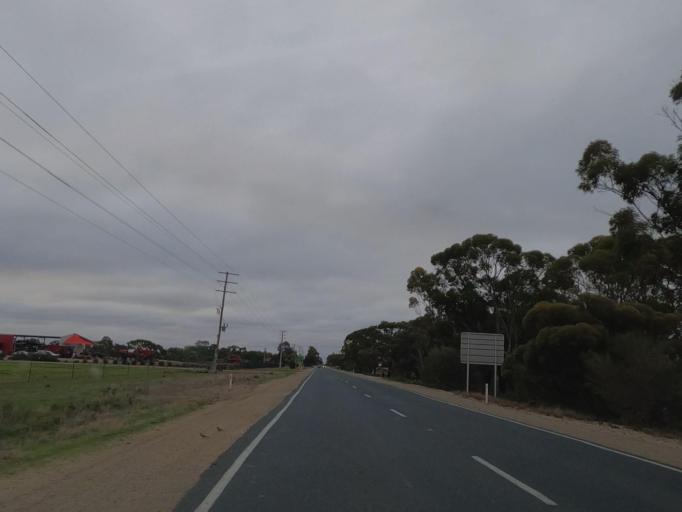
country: AU
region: Victoria
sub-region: Swan Hill
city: Swan Hill
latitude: -35.3889
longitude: 143.5690
